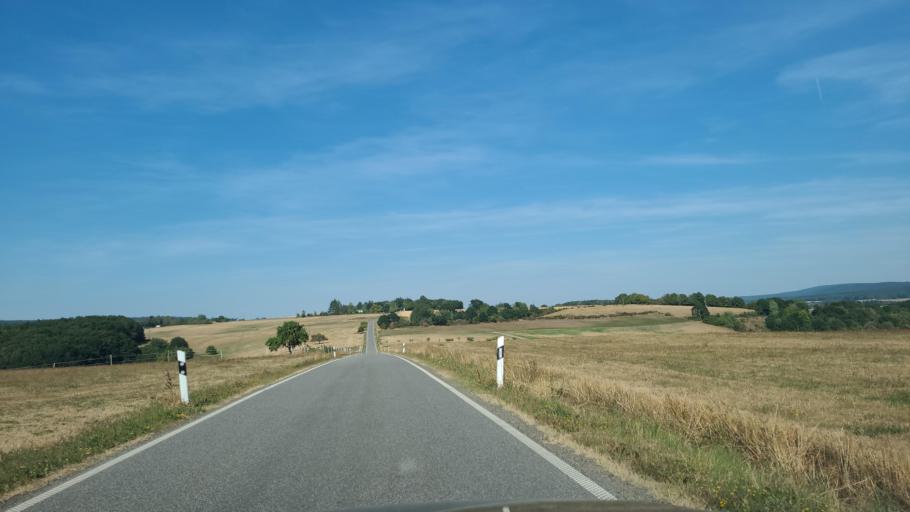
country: DE
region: Rheinland-Pfalz
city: Luckenburg
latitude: 49.7332
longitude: 6.9589
